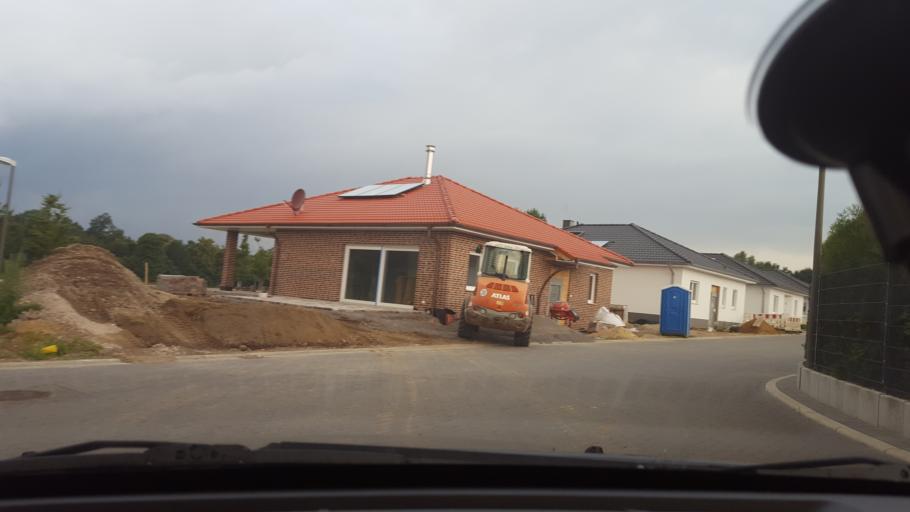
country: DE
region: North Rhine-Westphalia
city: Marl
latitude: 51.6537
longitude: 7.1408
